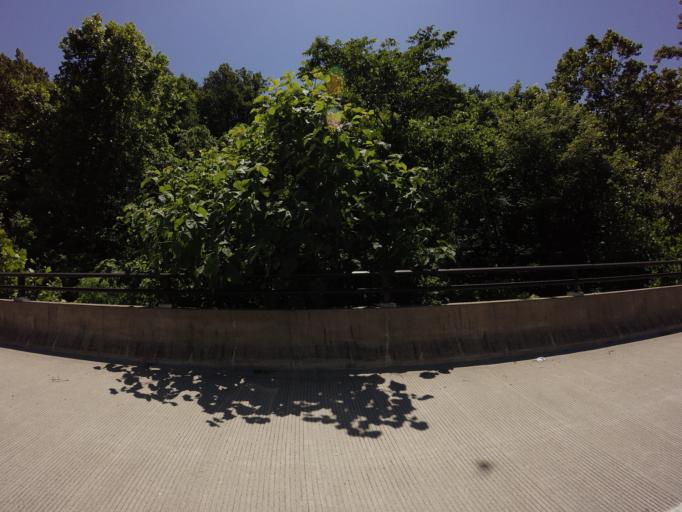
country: US
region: West Virginia
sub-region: Jefferson County
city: Bolivar
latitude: 39.3190
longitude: -77.7397
